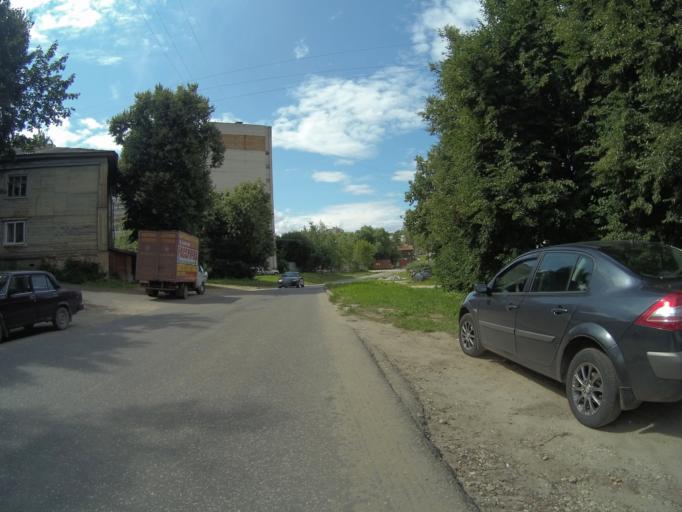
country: RU
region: Vladimir
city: Vladimir
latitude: 56.1242
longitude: 40.3825
